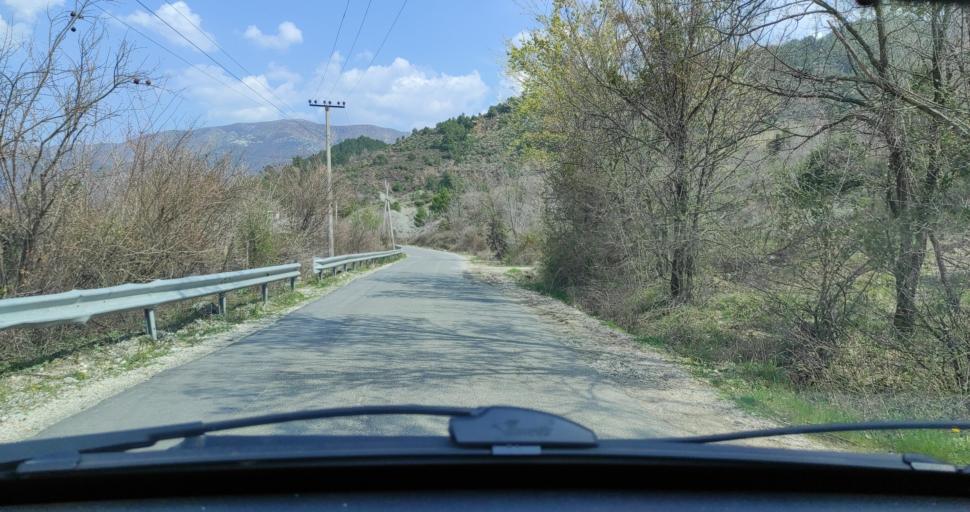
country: AL
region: Lezhe
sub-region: Rrethi i Lezhes
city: Kallmeti i Madh
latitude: 41.8514
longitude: 19.6928
